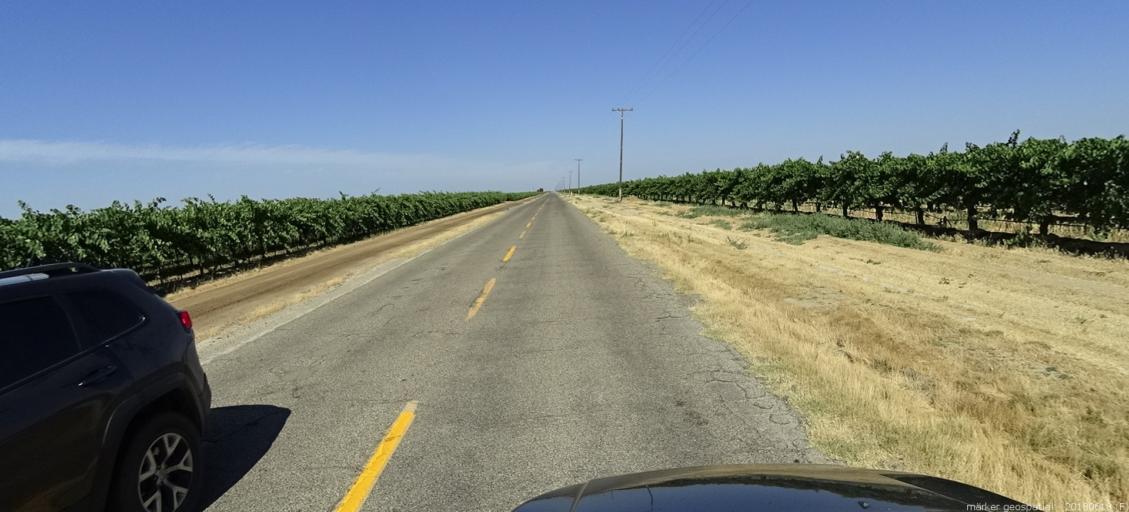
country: US
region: California
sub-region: Madera County
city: Parkwood
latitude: 36.8366
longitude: -120.1992
